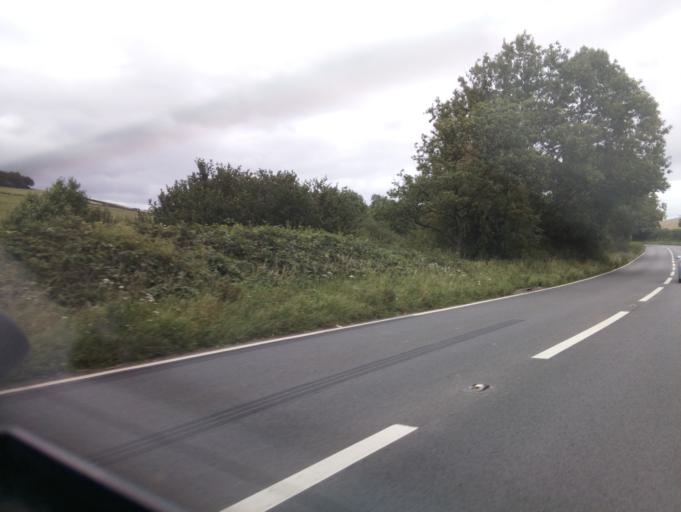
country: GB
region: England
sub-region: Devon
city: Totnes
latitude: 50.4297
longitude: -3.6495
